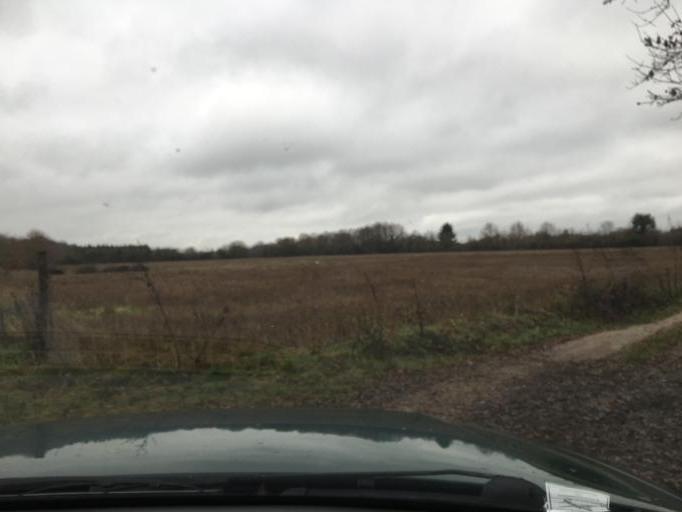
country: FR
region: Centre
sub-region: Departement du Loiret
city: Olivet
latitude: 47.8514
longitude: 1.8772
